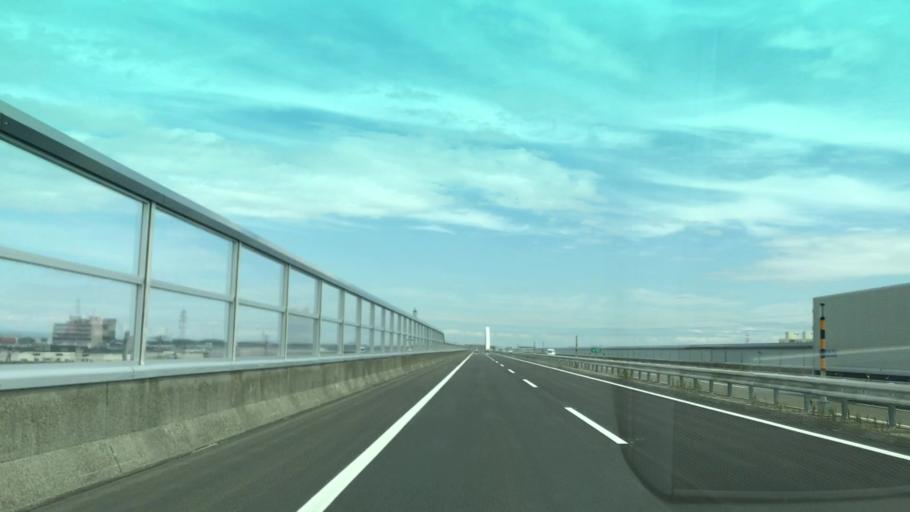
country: JP
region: Hokkaido
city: Sapporo
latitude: 43.0957
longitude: 141.2923
